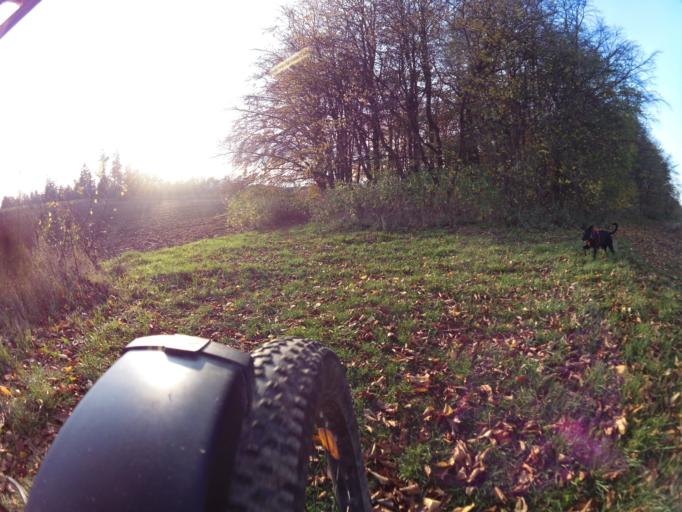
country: PL
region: Pomeranian Voivodeship
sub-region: Powiat pucki
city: Krokowa
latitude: 54.7700
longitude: 18.1778
